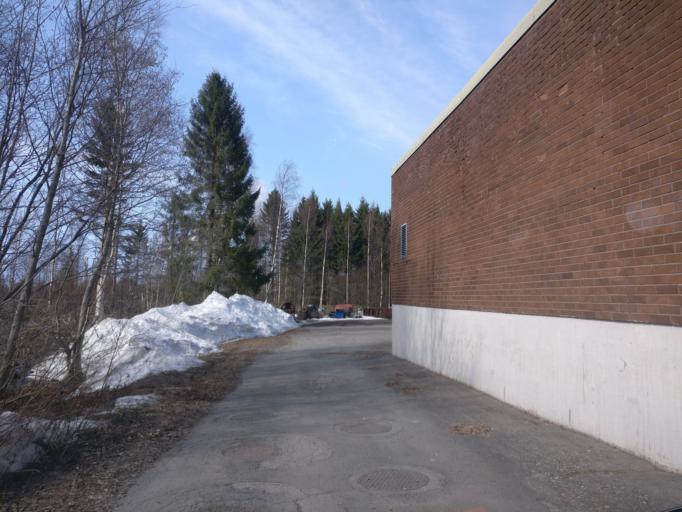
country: FI
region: Lapland
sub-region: Kemi-Tornio
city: Kemi
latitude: 65.7566
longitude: 24.5479
